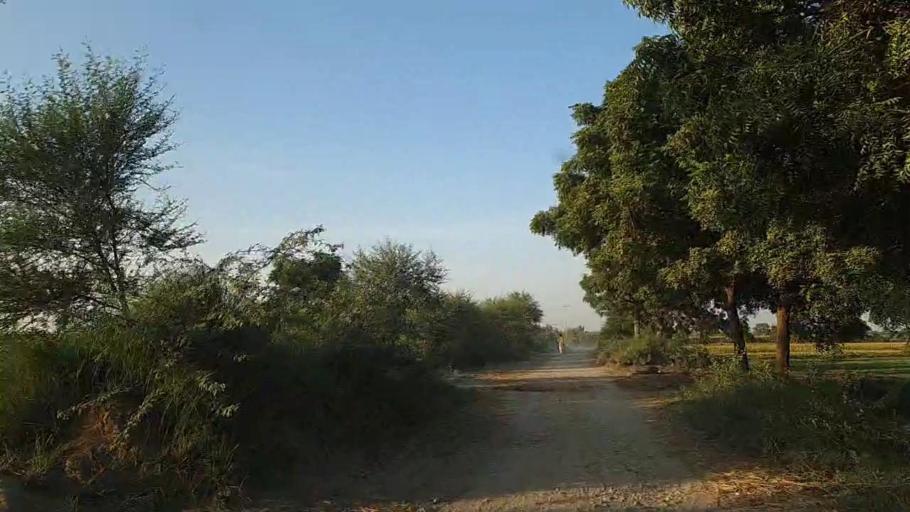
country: PK
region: Sindh
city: Mirpur Batoro
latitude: 24.7204
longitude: 68.2139
